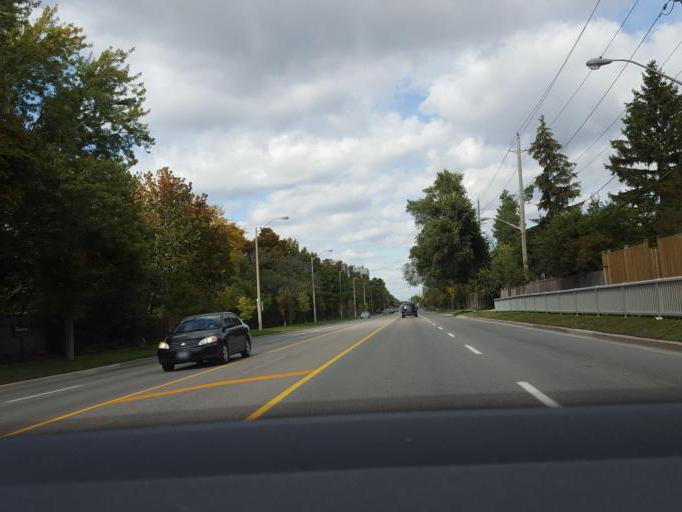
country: CA
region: Ontario
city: Willowdale
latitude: 43.7469
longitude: -79.3587
